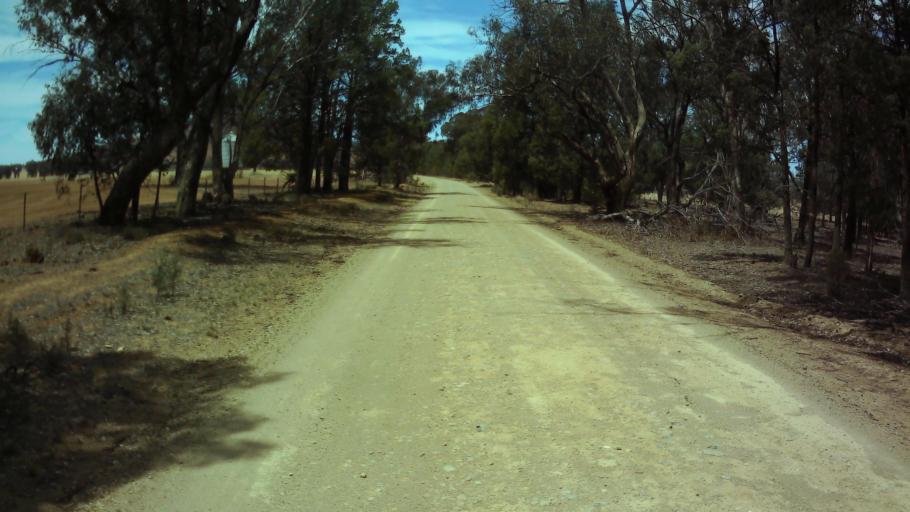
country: AU
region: New South Wales
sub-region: Weddin
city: Grenfell
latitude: -33.7622
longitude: 148.1287
